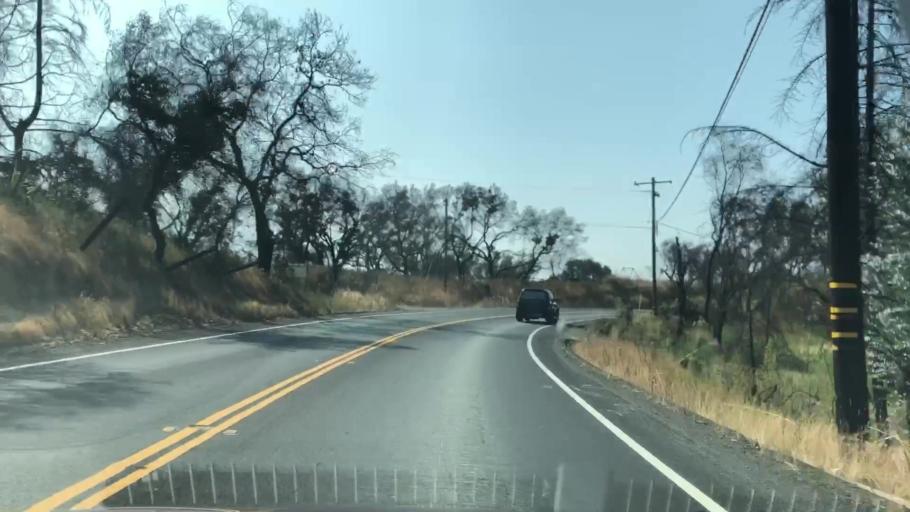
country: US
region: California
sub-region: Sonoma County
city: Larkfield-Wikiup
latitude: 38.5218
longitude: -122.7185
